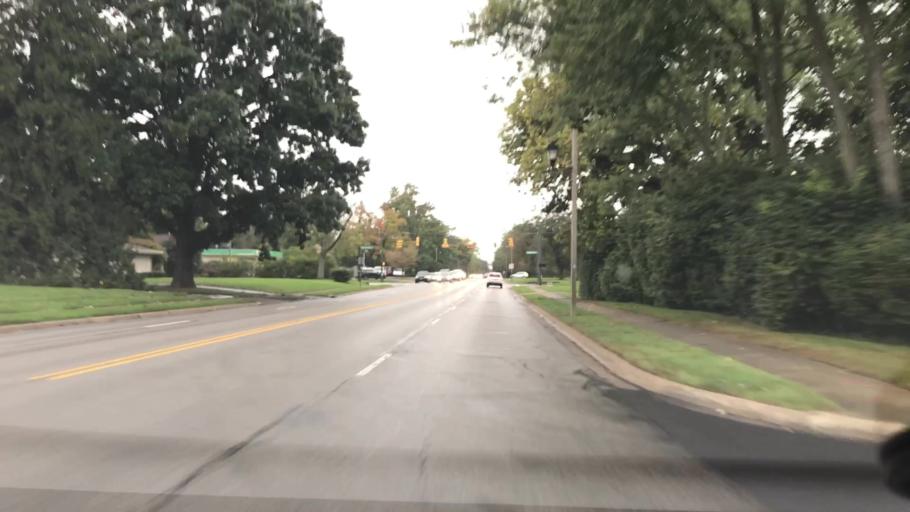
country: US
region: Ohio
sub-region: Franklin County
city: Upper Arlington
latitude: 40.0294
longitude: -83.0705
